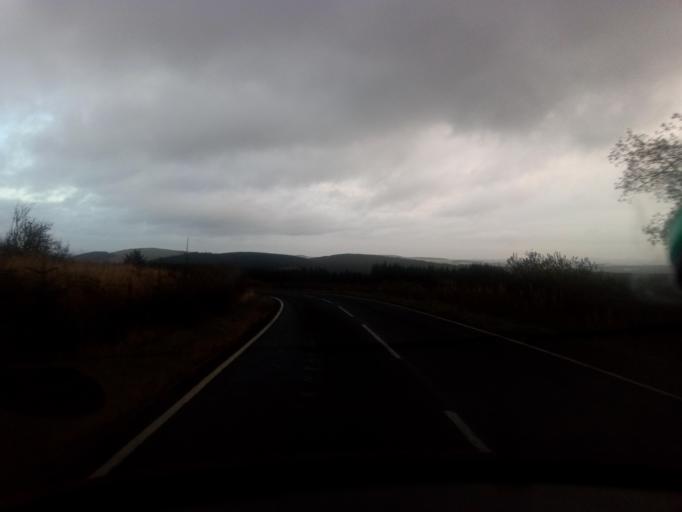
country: GB
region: Scotland
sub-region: The Scottish Borders
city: Hawick
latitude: 55.3244
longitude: -2.6465
